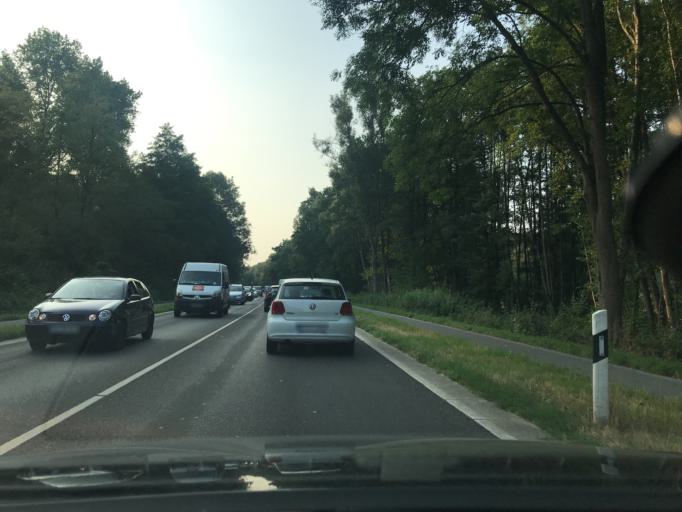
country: DE
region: North Rhine-Westphalia
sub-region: Regierungsbezirk Dusseldorf
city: Erkrath
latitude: 51.2086
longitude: 6.8776
